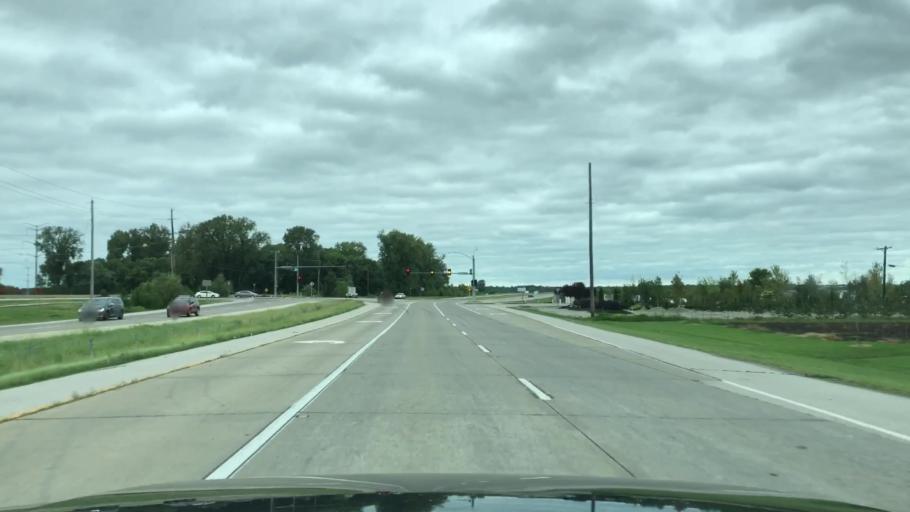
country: US
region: Missouri
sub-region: Saint Charles County
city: Saint Charles
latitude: 38.7306
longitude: -90.4855
